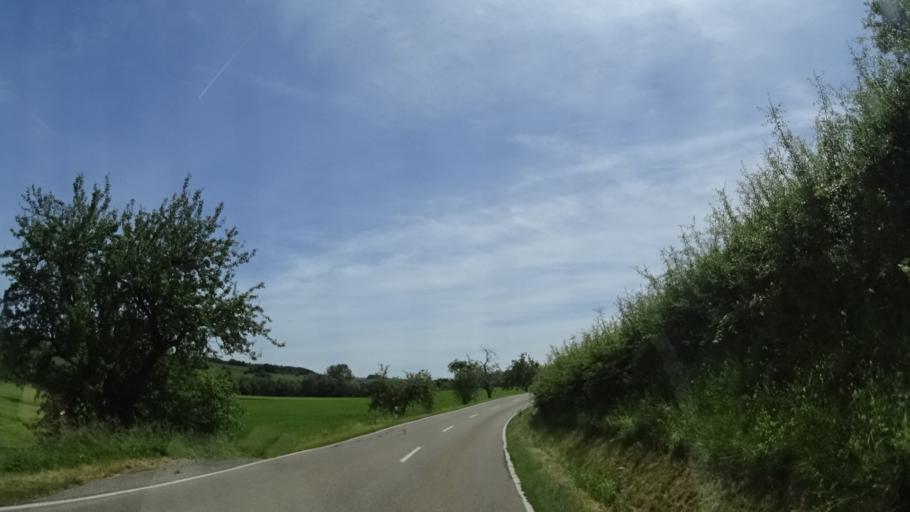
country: DE
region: Baden-Wuerttemberg
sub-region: Regierungsbezirk Stuttgart
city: Buhlertann
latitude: 49.0308
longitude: 9.9050
